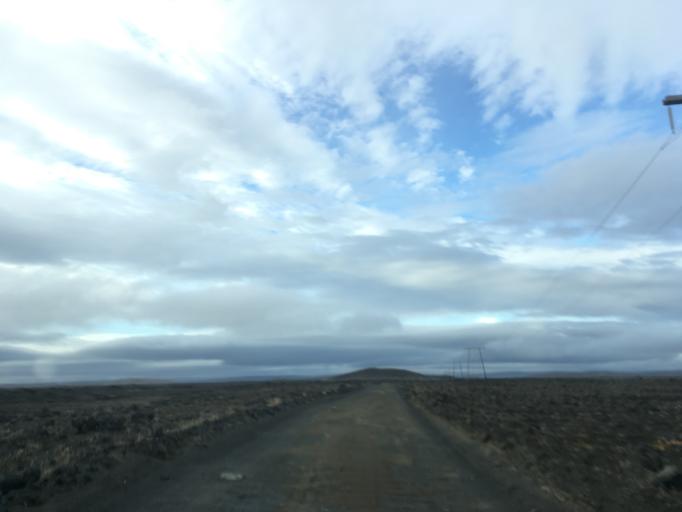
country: IS
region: South
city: Vestmannaeyjar
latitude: 64.1105
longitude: -19.1109
